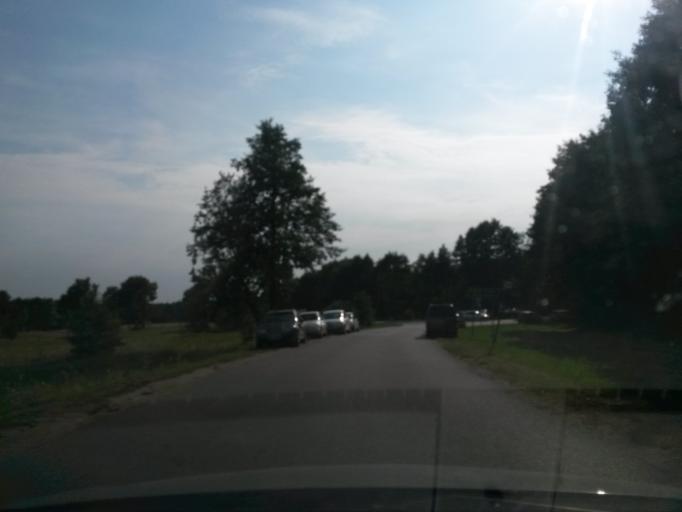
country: PL
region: Masovian Voivodeship
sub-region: Powiat sierpecki
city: Szczutowo
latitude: 52.9499
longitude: 19.5851
